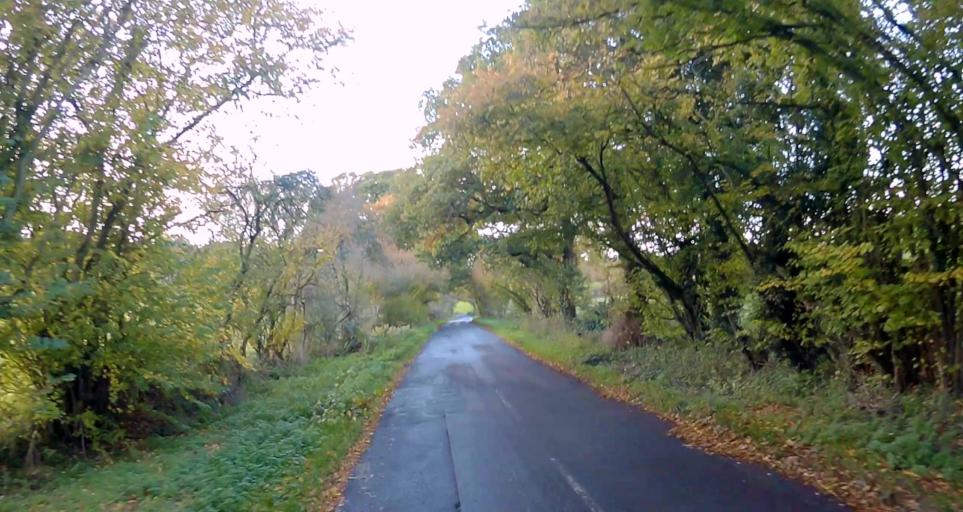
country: GB
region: England
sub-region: Hampshire
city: Basingstoke
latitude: 51.1907
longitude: -1.0791
